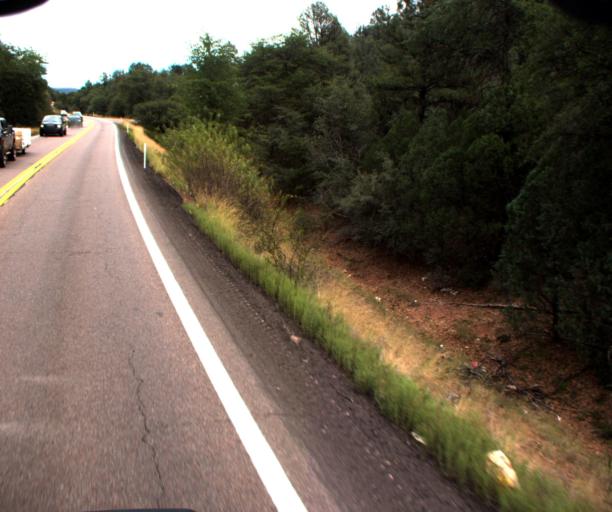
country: US
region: Arizona
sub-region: Gila County
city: Star Valley
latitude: 34.2606
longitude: -111.2501
